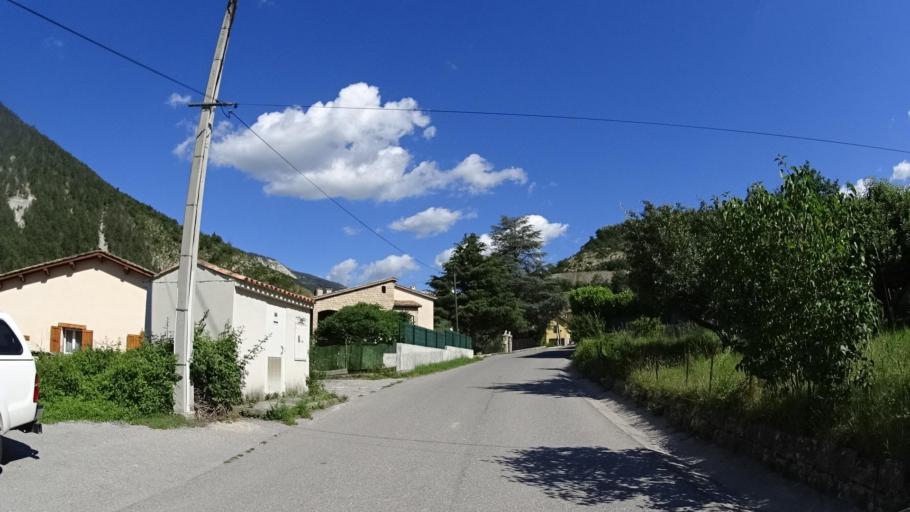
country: FR
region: Provence-Alpes-Cote d'Azur
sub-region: Departement des Alpes-de-Haute-Provence
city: Annot
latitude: 44.0018
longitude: 6.6426
